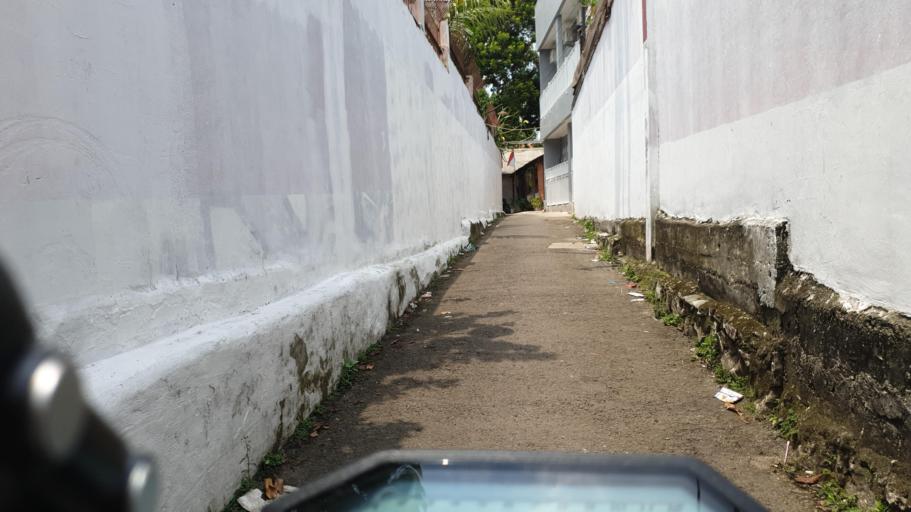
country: ID
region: West Java
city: Depok
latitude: -6.3317
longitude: 106.8291
